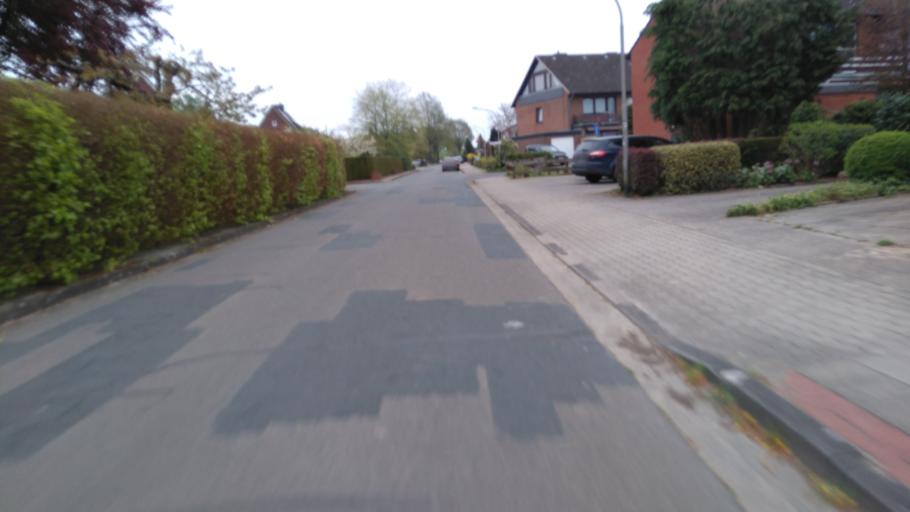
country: DE
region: Lower Saxony
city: Harsefeld
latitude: 53.4532
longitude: 9.5100
